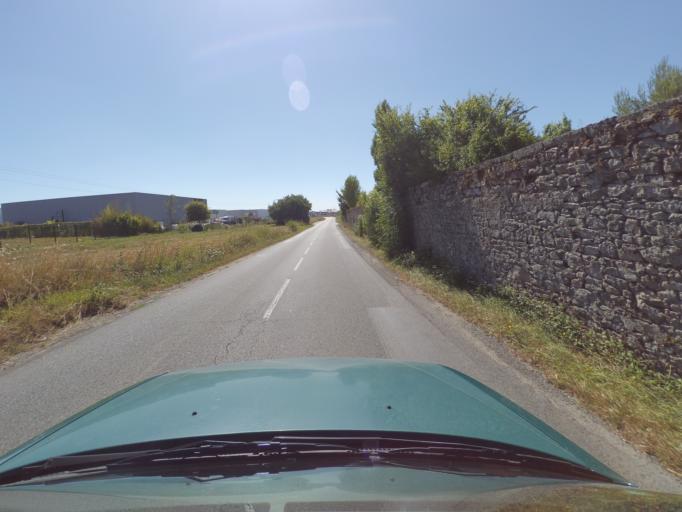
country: FR
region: Pays de la Loire
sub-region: Departement de la Loire-Atlantique
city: Le Bignon
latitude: 47.1224
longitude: -1.5084
